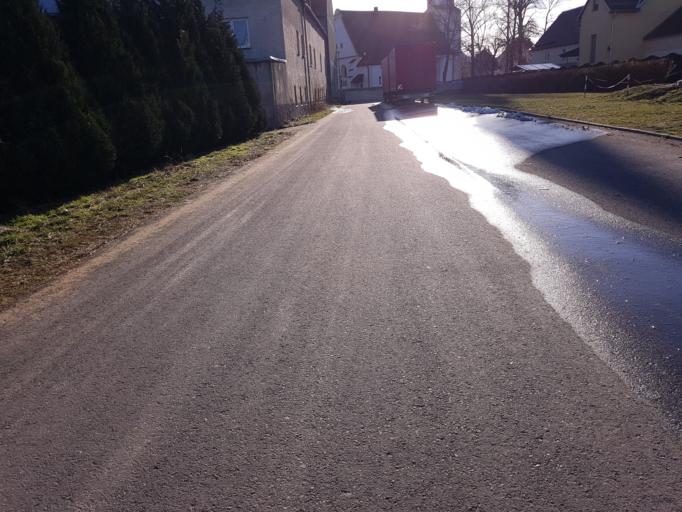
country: DE
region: Brandenburg
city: Groden
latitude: 51.4088
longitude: 13.5716
